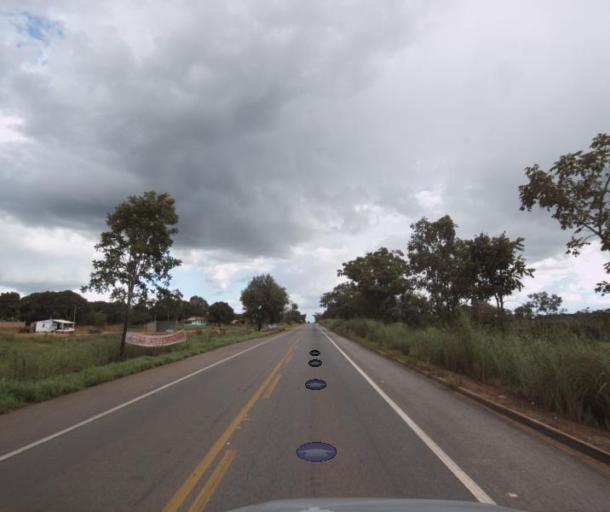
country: BR
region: Goias
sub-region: Porangatu
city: Porangatu
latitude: -13.3144
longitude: -49.1178
